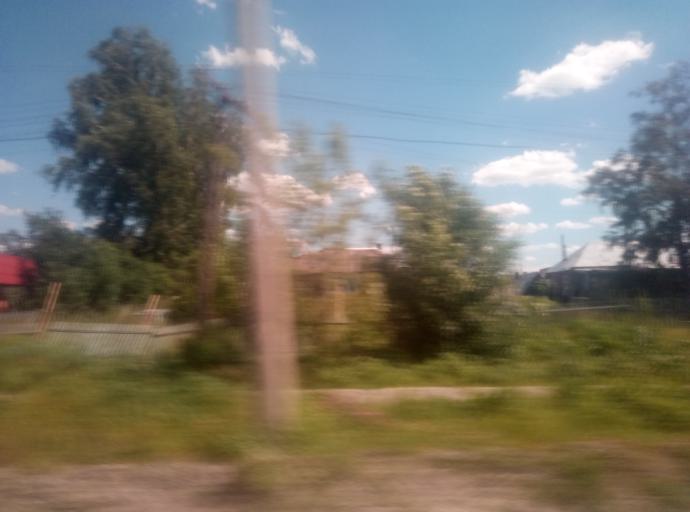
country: RU
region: Tula
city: Kireyevsk
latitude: 53.9841
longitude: 37.9331
